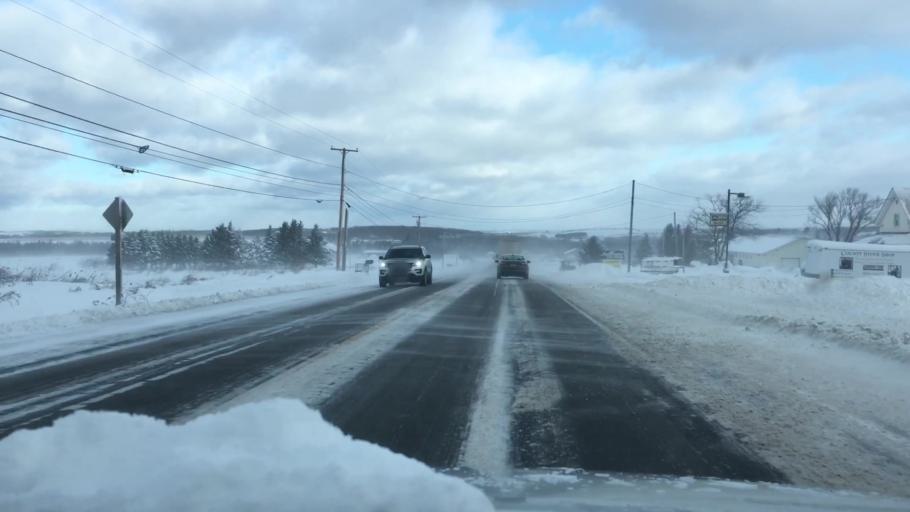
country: US
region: Maine
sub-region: Aroostook County
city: Caribou
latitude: 46.7941
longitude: -67.9913
